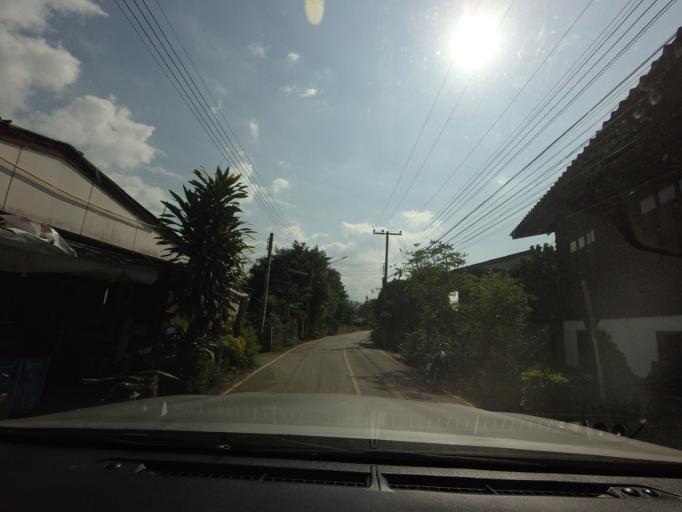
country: TH
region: Mae Hong Son
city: Wiang Nuea
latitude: 19.3948
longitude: 98.4435
